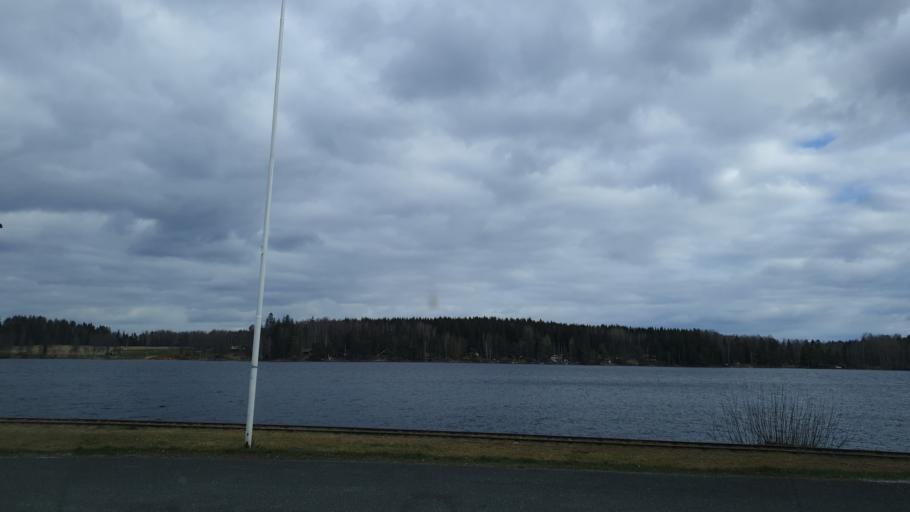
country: SE
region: OErebro
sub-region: Nora Kommun
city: Nora
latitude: 59.5165
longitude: 15.0424
